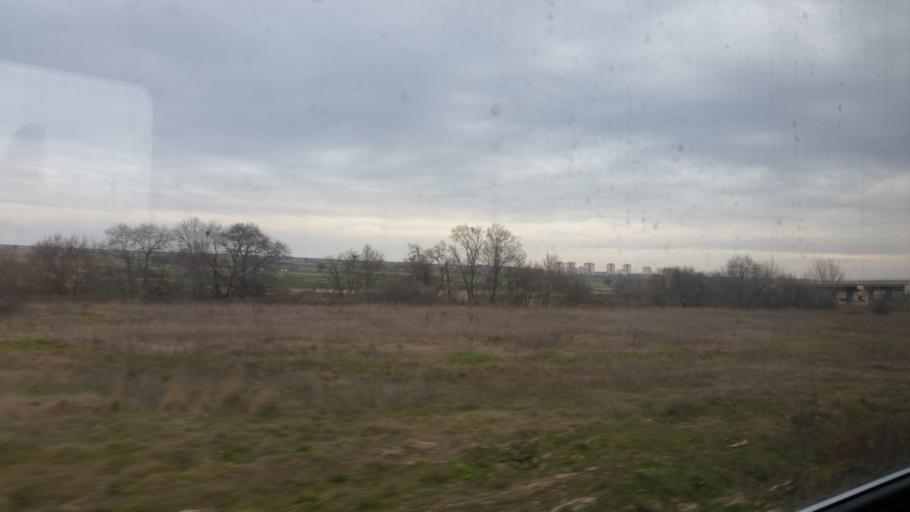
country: TR
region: Tekirdag
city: Velimese
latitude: 41.2350
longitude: 27.8679
